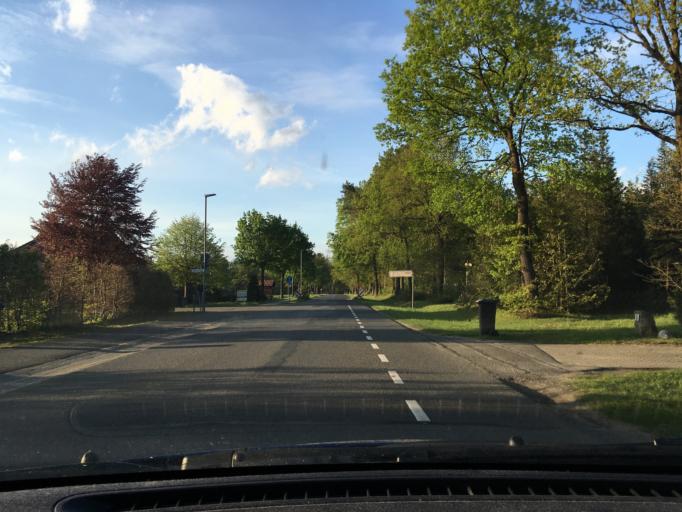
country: DE
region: Lower Saxony
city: Wietzendorf
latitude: 52.9305
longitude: 9.9805
